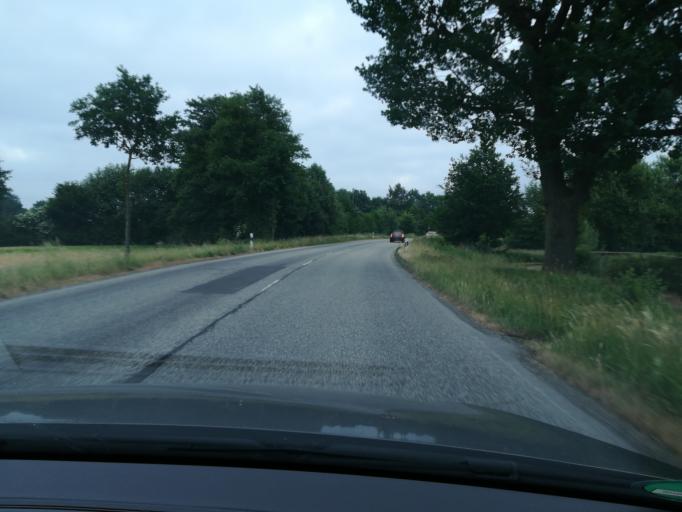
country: DE
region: Schleswig-Holstein
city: Siek
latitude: 53.6422
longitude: 10.3024
